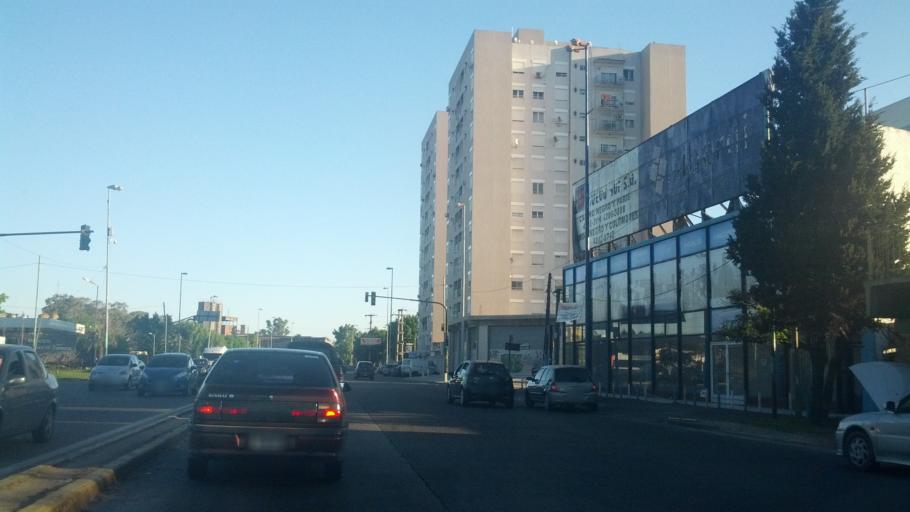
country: AR
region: Buenos Aires
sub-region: Partido de Lomas de Zamora
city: Lomas de Zamora
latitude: -34.7595
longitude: -58.4314
